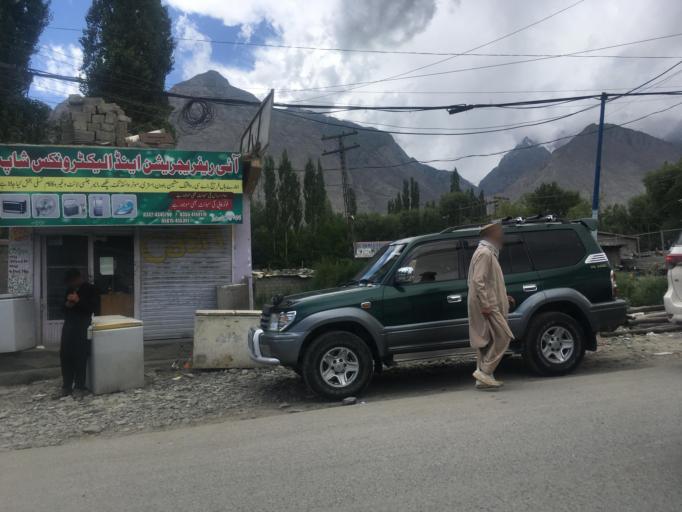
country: PK
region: Gilgit-Baltistan
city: Skardu
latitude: 35.2949
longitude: 75.6106
